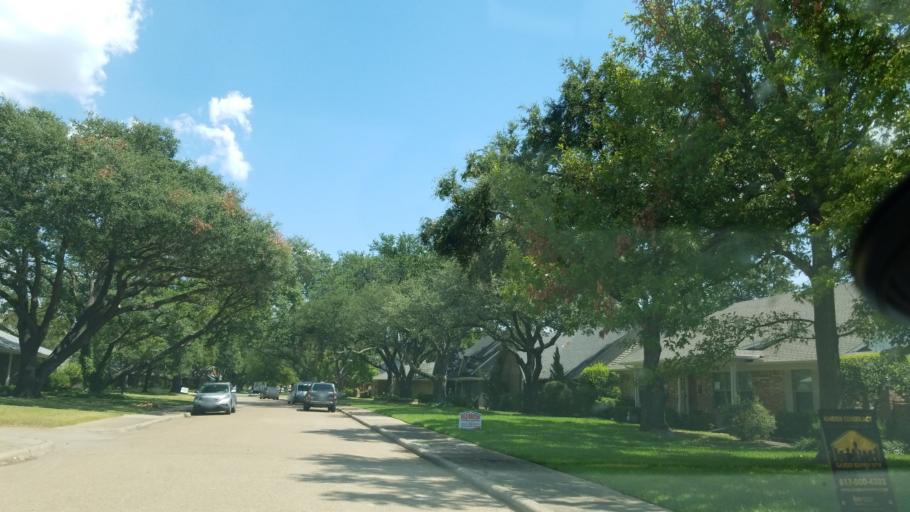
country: US
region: Texas
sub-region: Dallas County
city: Richardson
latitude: 32.8896
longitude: -96.7169
